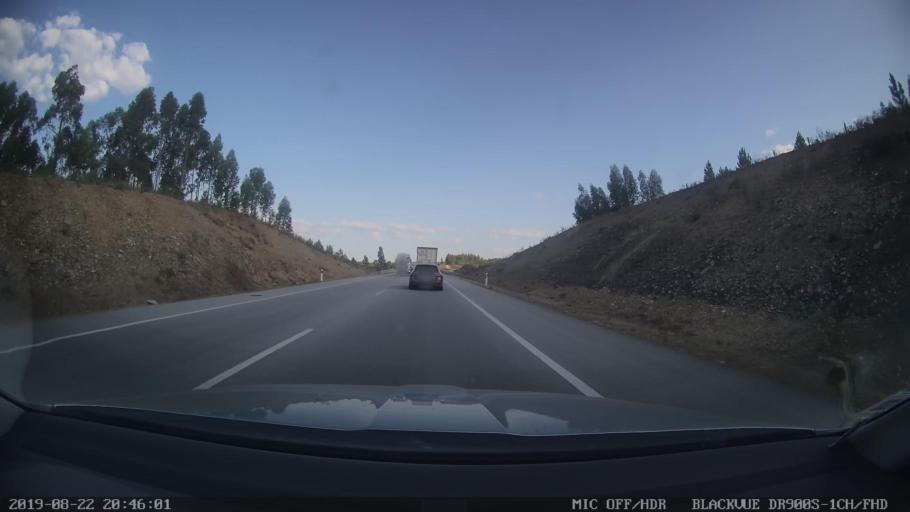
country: PT
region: Castelo Branco
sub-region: Proenca-A-Nova
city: Proenca-a-Nova
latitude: 39.7226
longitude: -7.8724
